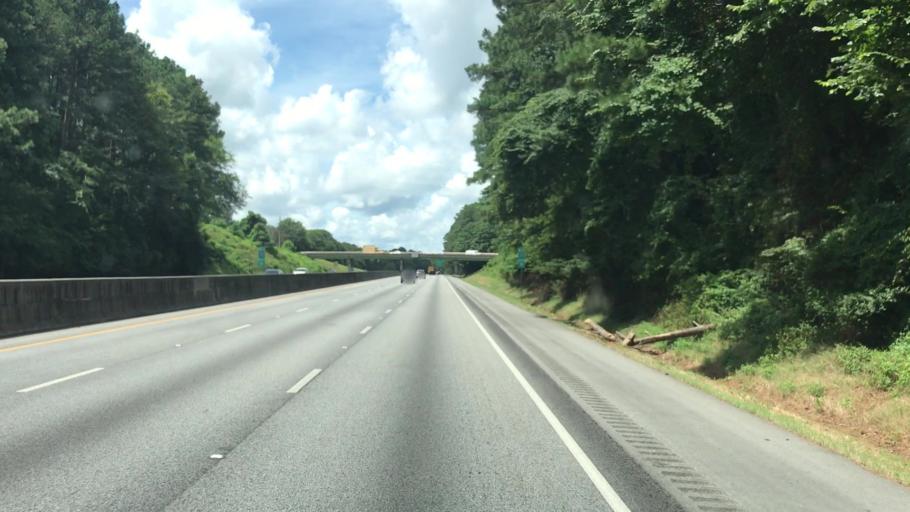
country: US
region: Georgia
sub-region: Newton County
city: Oxford
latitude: 33.6116
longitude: -83.8650
